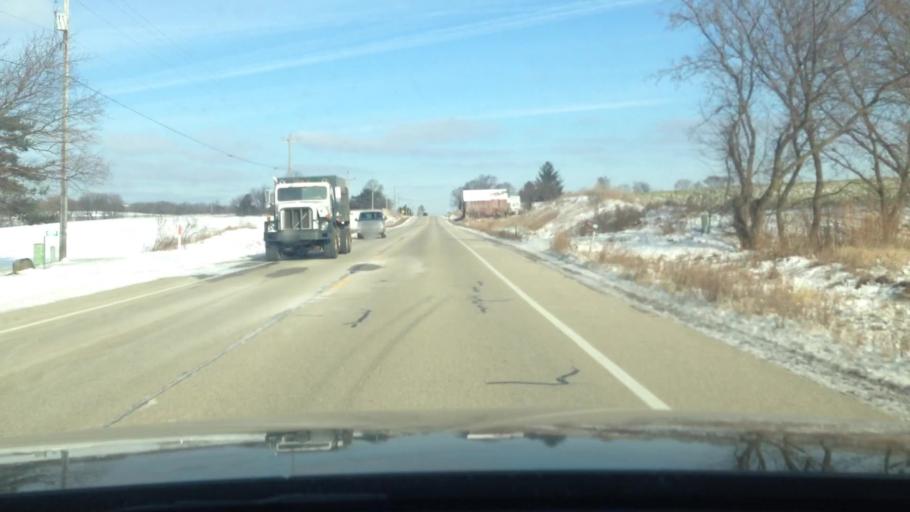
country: US
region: Wisconsin
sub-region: Walworth County
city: East Troy
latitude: 42.7631
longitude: -88.4065
